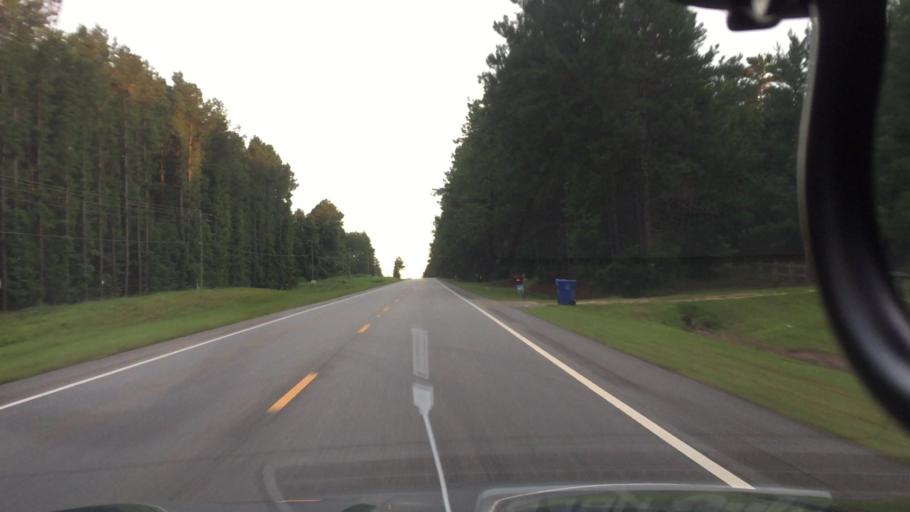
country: US
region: Alabama
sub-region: Coffee County
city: New Brockton
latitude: 31.5217
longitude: -85.9173
